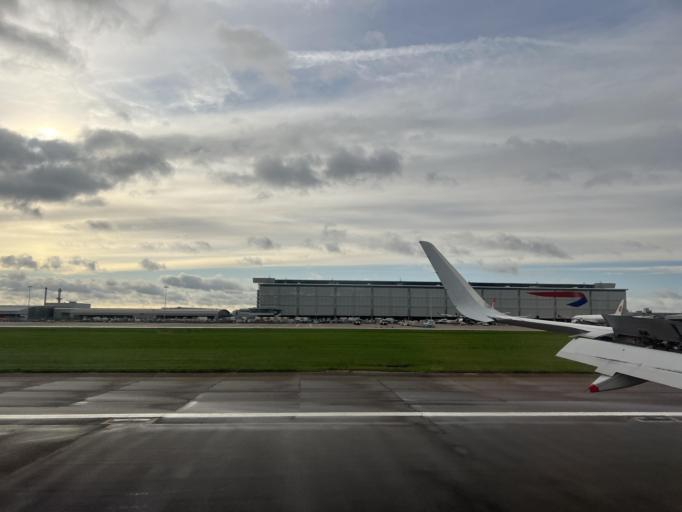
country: GB
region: England
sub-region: Greater London
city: West Drayton
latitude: 51.4645
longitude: -0.4634
